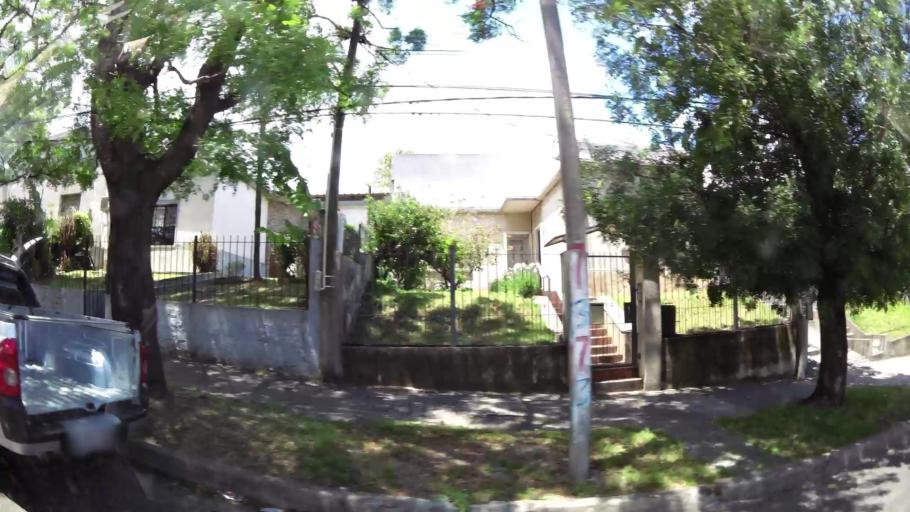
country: UY
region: Montevideo
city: Montevideo
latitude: -34.8560
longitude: -56.1837
